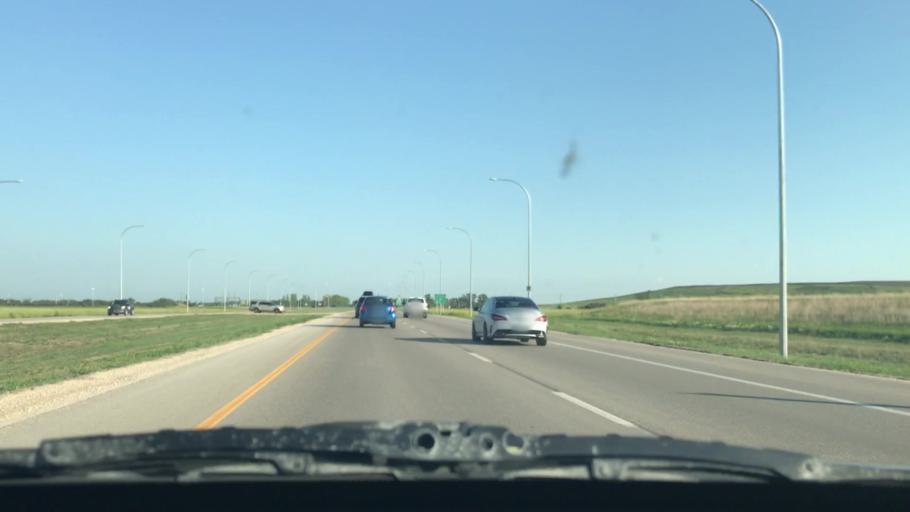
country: CA
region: Manitoba
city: Winnipeg
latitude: 49.7735
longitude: -97.1857
